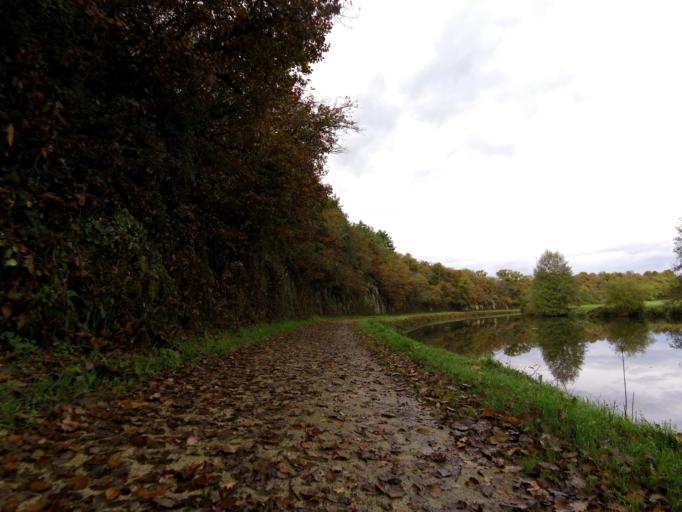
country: FR
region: Brittany
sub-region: Departement d'Ille-et-Vilaine
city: Bourg-des-Comptes
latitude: 47.9274
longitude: -1.7602
